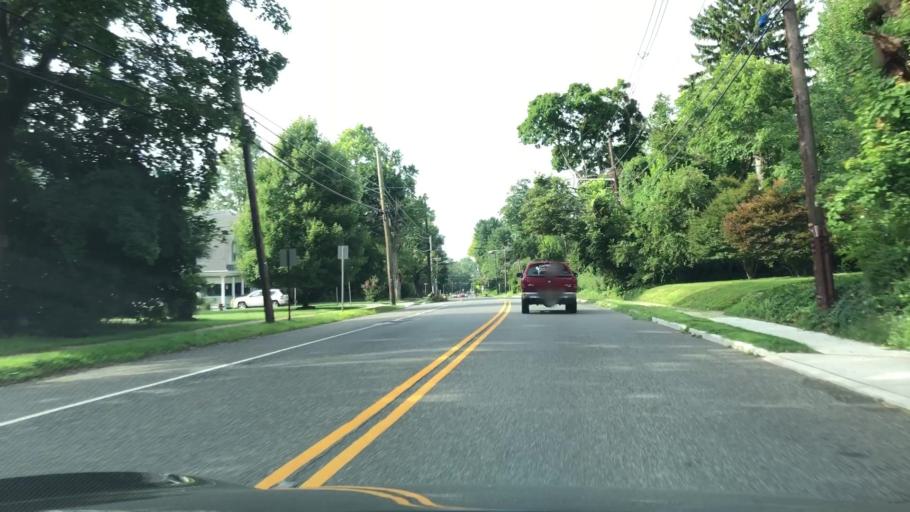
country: US
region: New Jersey
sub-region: Mercer County
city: Prospect Park
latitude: 40.2597
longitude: -74.7419
